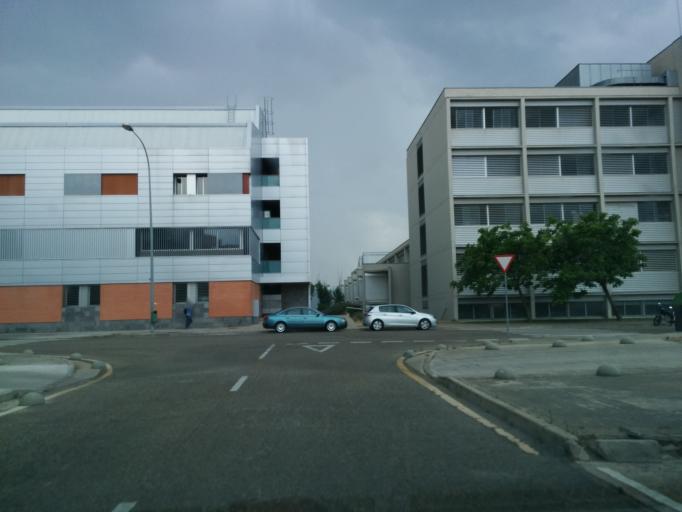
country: ES
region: Aragon
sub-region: Provincia de Zaragoza
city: Almozara
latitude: 41.6845
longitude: -0.8882
